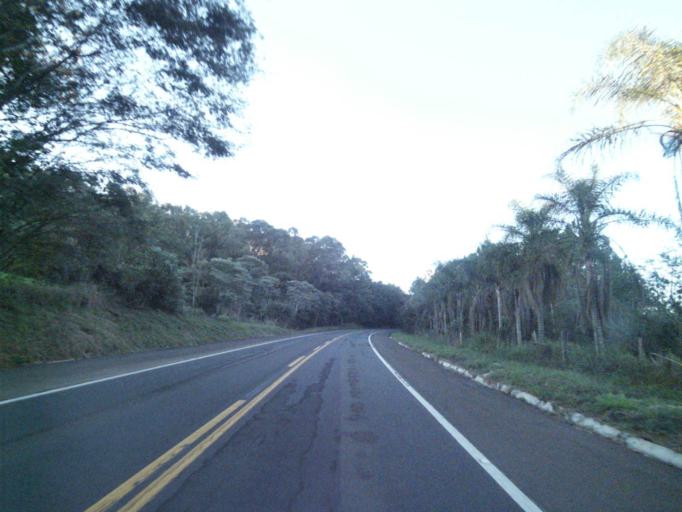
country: BR
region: Parana
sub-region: Faxinal
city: Faxinal
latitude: -23.7808
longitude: -51.1558
